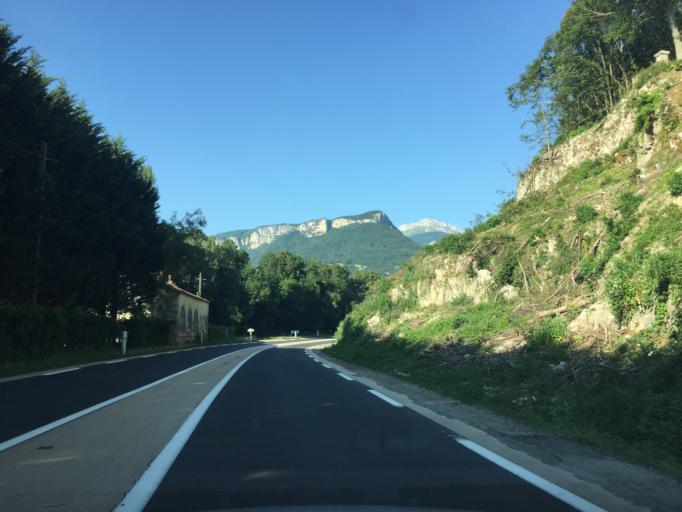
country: FR
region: Rhone-Alpes
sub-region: Departement de l'Isere
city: Veurey-Voroize
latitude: 45.3005
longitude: 5.5996
